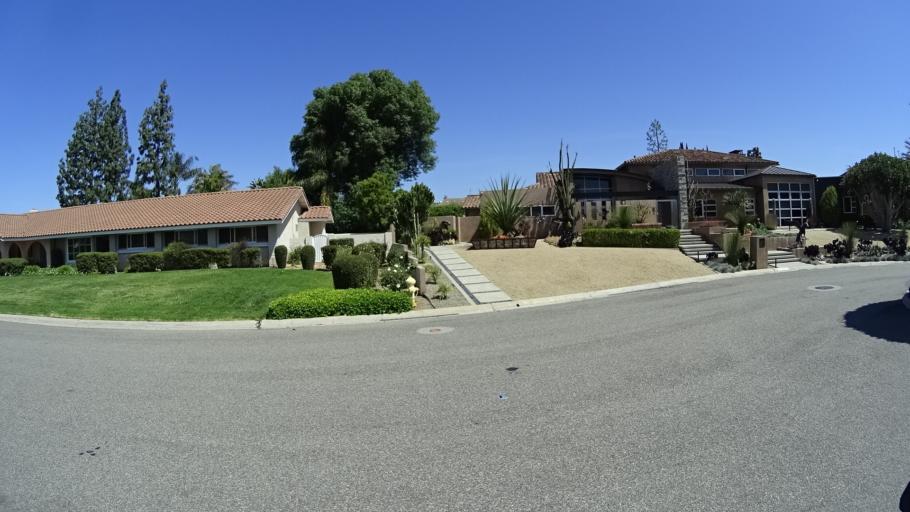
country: US
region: California
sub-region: Orange County
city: Villa Park
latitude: 33.8156
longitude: -117.8075
